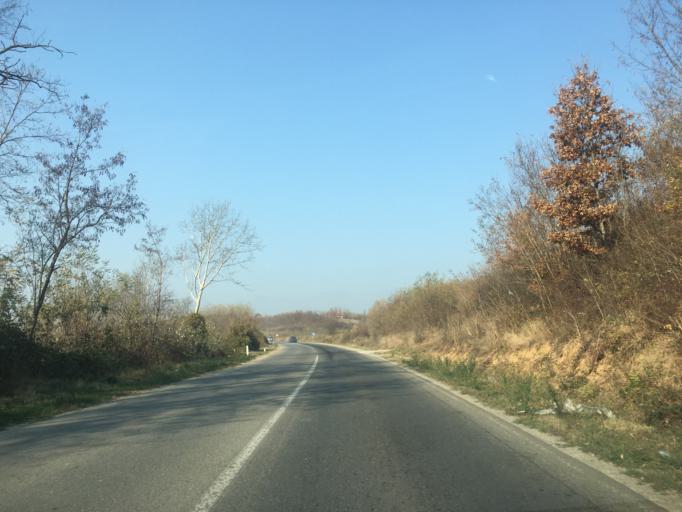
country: XK
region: Pec
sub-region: Komuna e Pejes
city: Kosuriq
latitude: 42.6394
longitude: 20.4271
